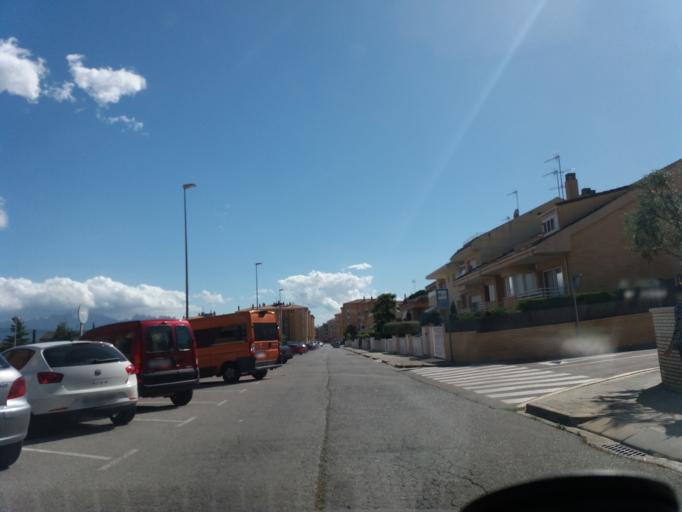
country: ES
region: Catalonia
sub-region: Provincia de Barcelona
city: Manresa
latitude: 41.7428
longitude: 1.8365
